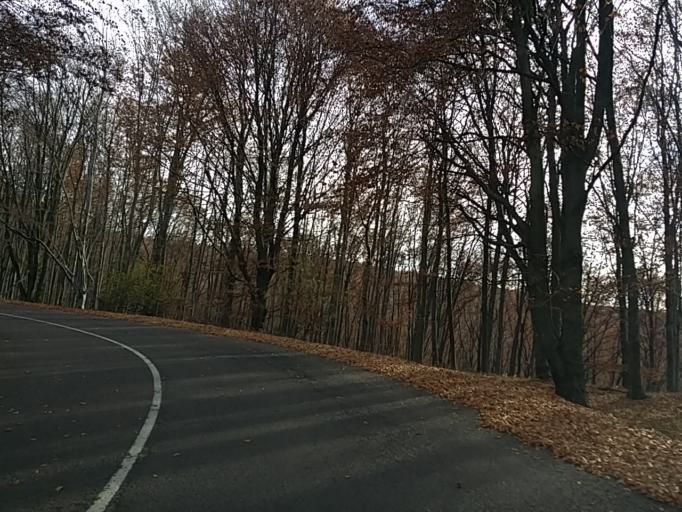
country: HU
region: Heves
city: Paradsasvar
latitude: 47.8681
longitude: 20.0026
